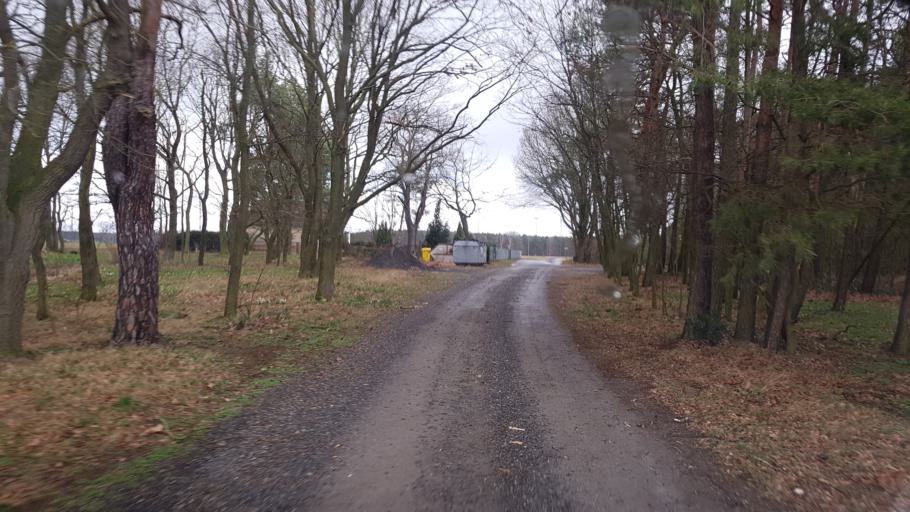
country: DE
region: Brandenburg
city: Sallgast
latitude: 51.6101
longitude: 13.8395
